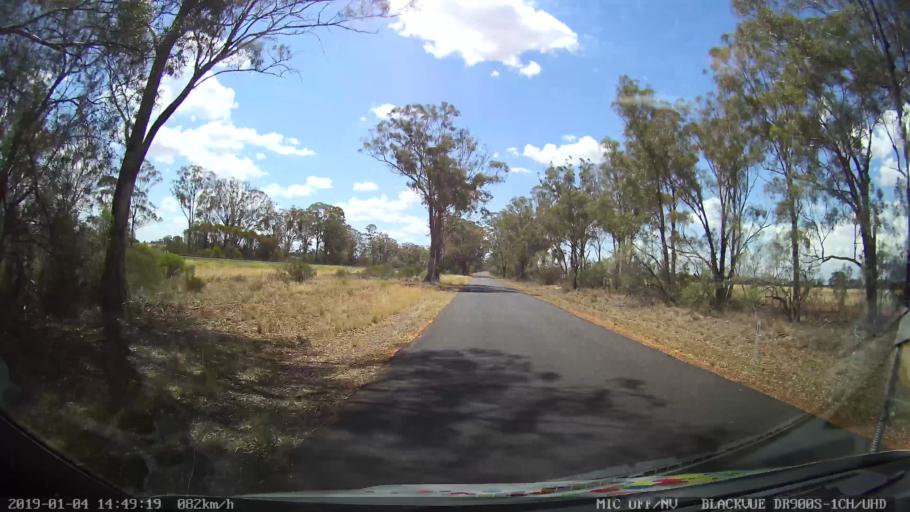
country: AU
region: New South Wales
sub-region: Dubbo Municipality
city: Dubbo
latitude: -32.0504
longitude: 148.6636
